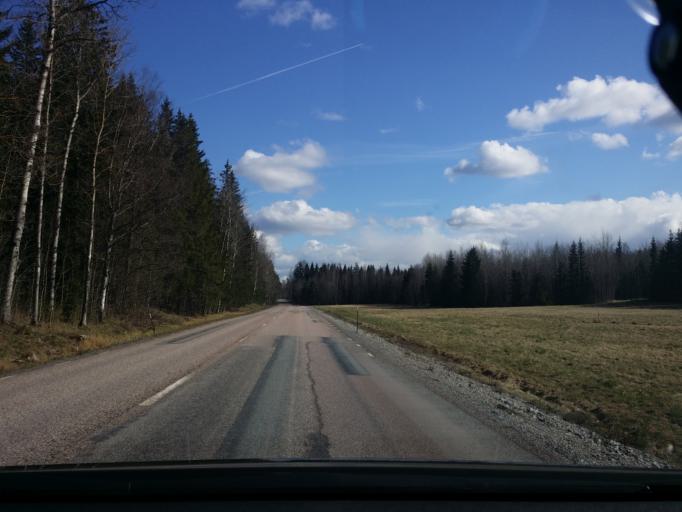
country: SE
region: Vaestmanland
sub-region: Sala Kommun
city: Sala
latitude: 59.9782
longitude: 16.4927
